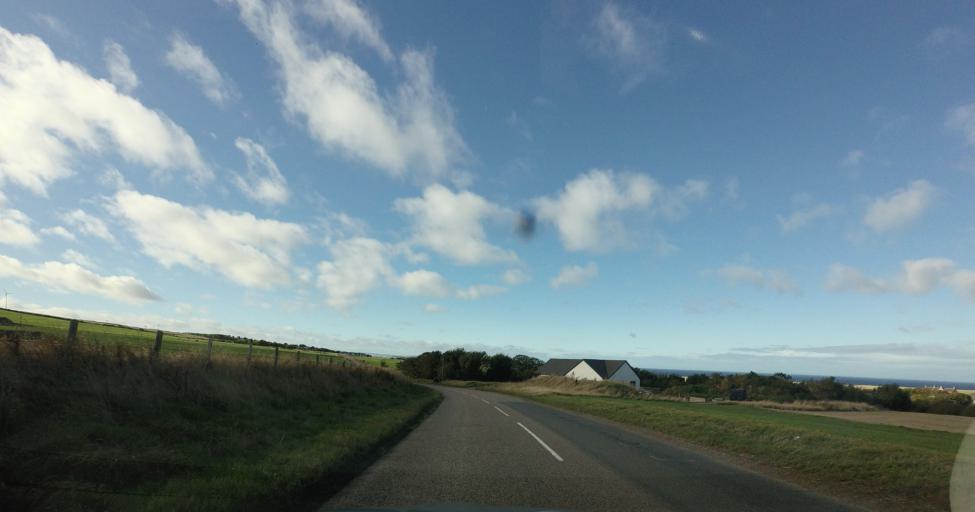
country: GB
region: Scotland
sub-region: Aberdeenshire
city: Macduff
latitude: 57.6639
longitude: -2.4255
